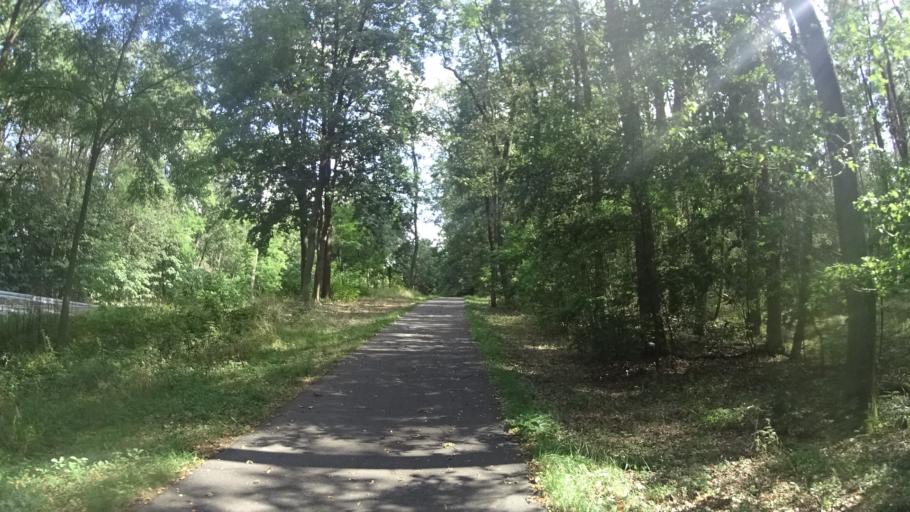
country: DE
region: Brandenburg
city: Rhinow
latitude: 52.7191
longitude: 12.3641
